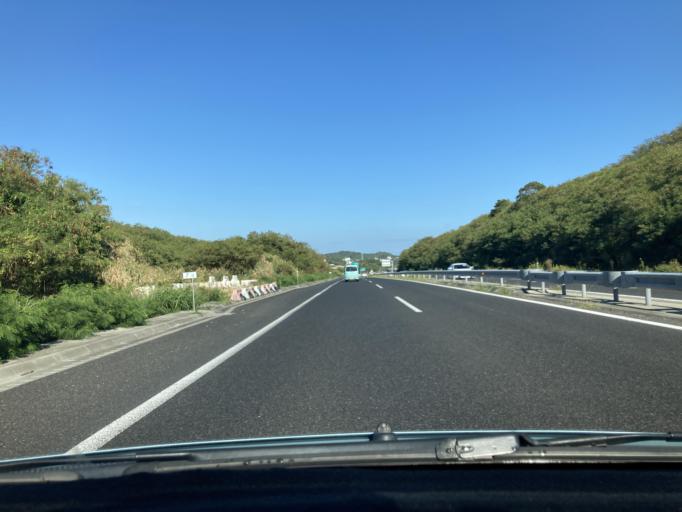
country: JP
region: Okinawa
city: Tomigusuku
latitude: 26.1760
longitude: 127.7072
